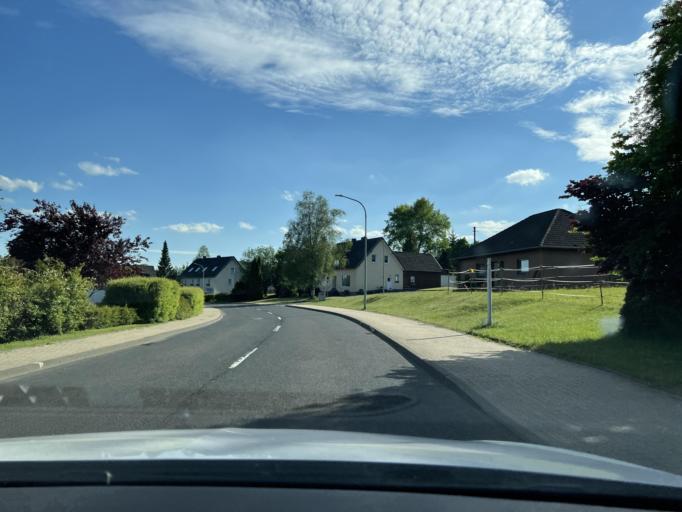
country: DE
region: North Rhine-Westphalia
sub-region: Regierungsbezirk Koln
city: Monschau
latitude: 50.5697
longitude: 6.2201
